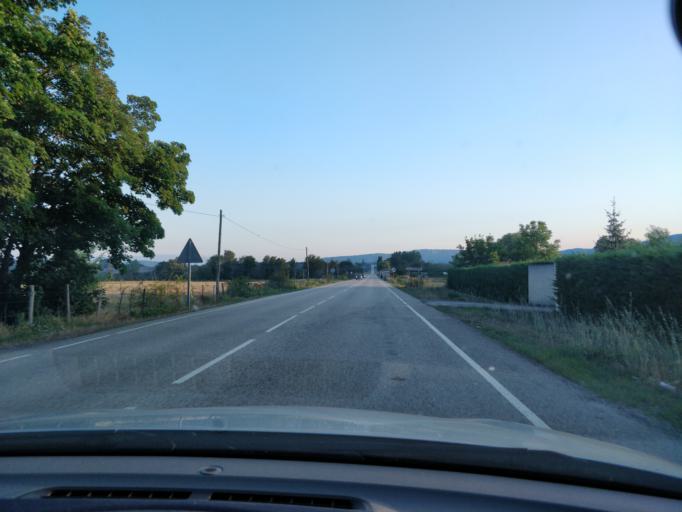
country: ES
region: Castille and Leon
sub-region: Provincia de Burgos
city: Espinosa de los Monteros
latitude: 43.0399
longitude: -3.4934
